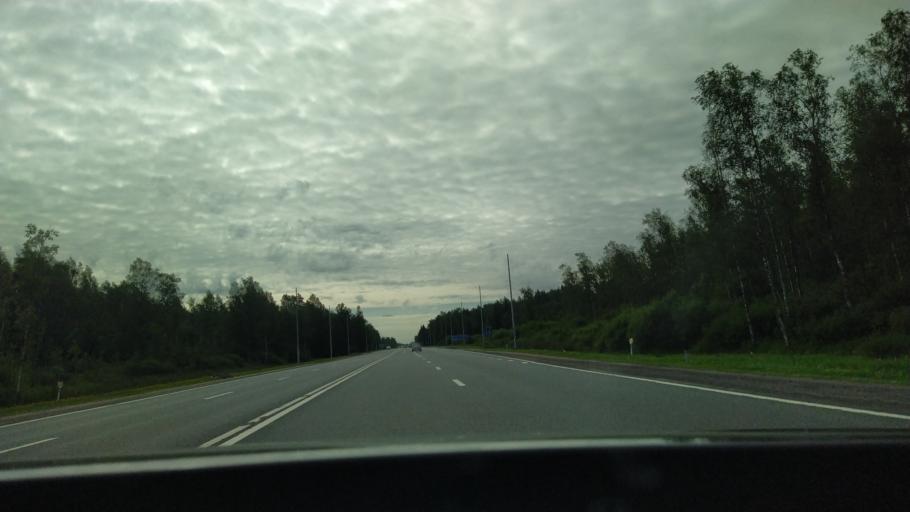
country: RU
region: Leningrad
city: Ul'yanovka
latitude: 59.5858
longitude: 30.7956
